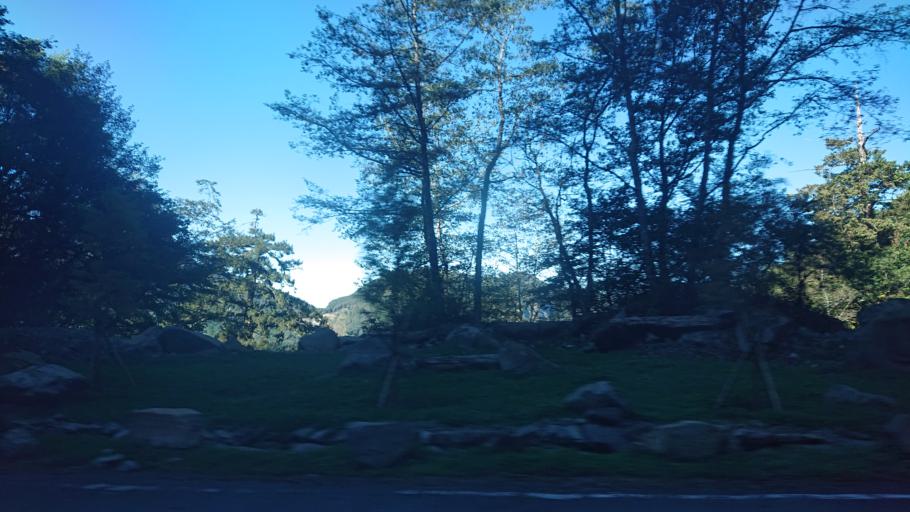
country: TW
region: Taiwan
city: Lugu
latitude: 23.4793
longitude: 120.8529
